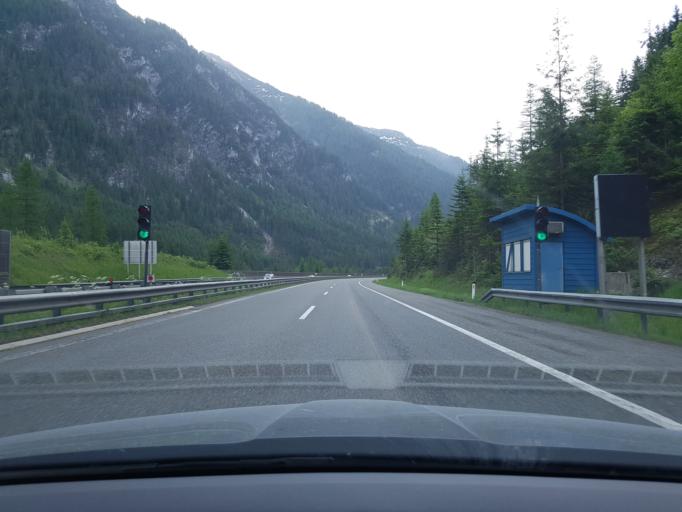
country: AT
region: Salzburg
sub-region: Politischer Bezirk Sankt Johann im Pongau
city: Flachau
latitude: 47.2815
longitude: 13.4080
